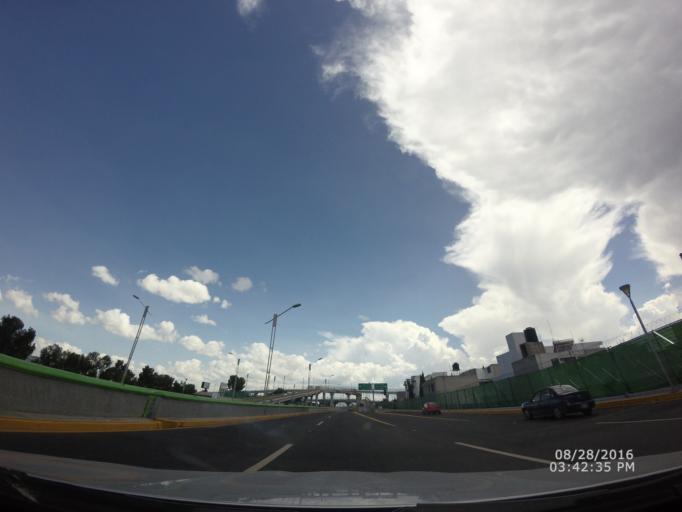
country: MX
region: Hidalgo
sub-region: Mineral de la Reforma
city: PRI Chacon
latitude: 20.0921
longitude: -98.7489
